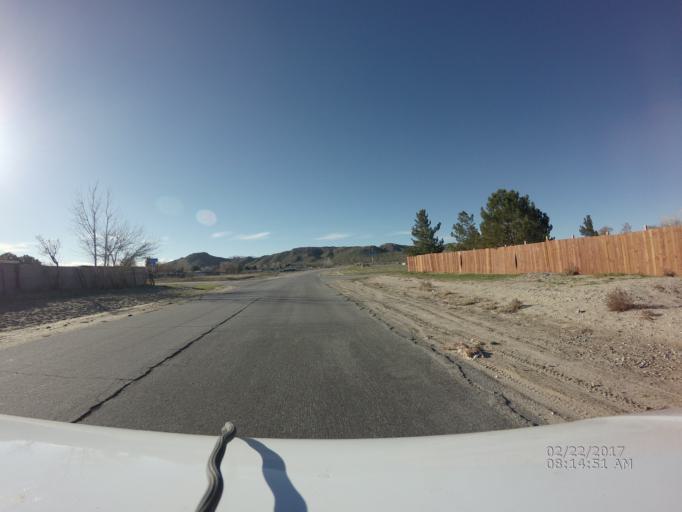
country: US
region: California
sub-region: Los Angeles County
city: Lake Los Angeles
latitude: 34.6206
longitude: -117.8447
